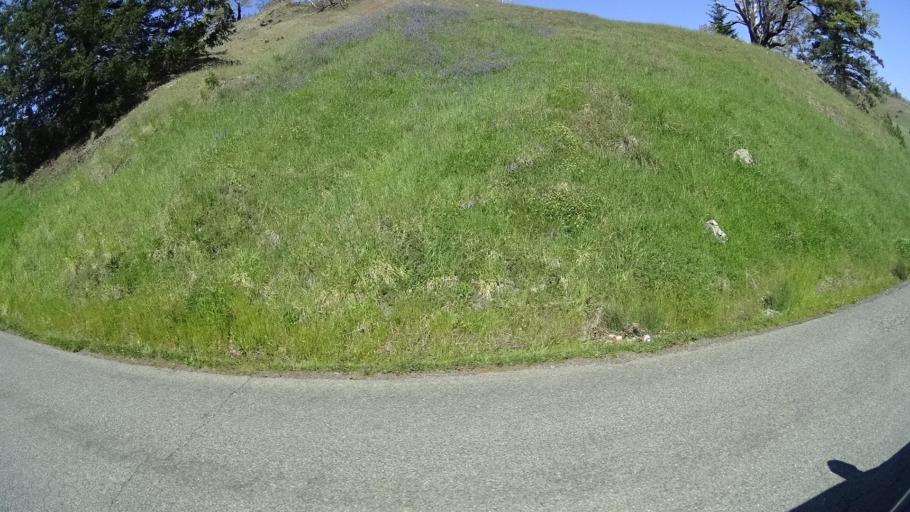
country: US
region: California
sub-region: Humboldt County
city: Redway
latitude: 40.1004
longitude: -123.6845
